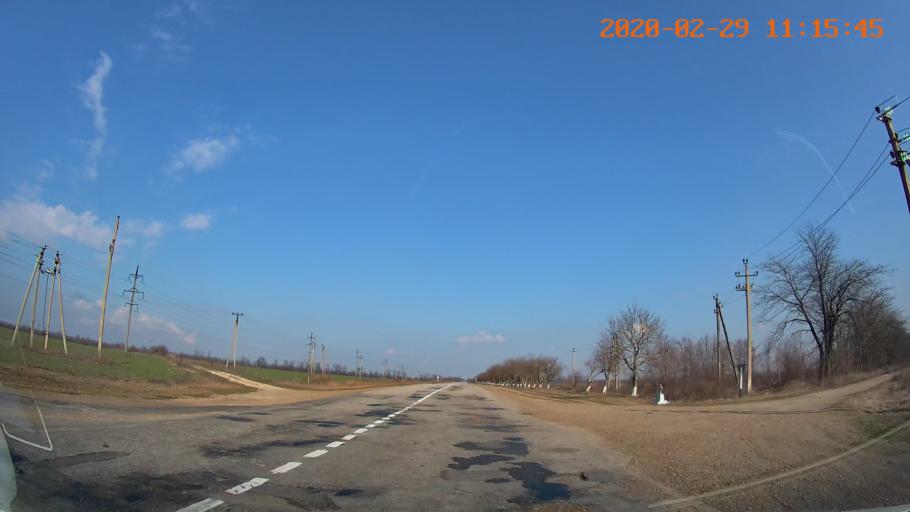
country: MD
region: Telenesti
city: Dubasari
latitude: 47.2989
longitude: 29.1659
